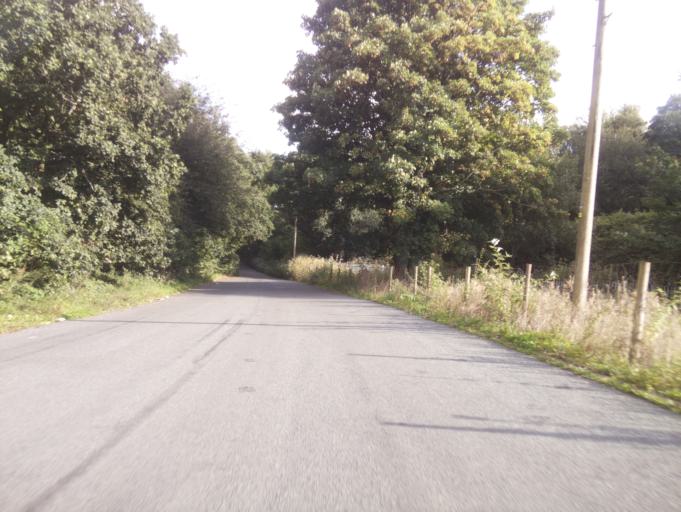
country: GB
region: Wales
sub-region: Caerphilly County Borough
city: Abertridwr
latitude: 51.5710
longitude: -3.2947
